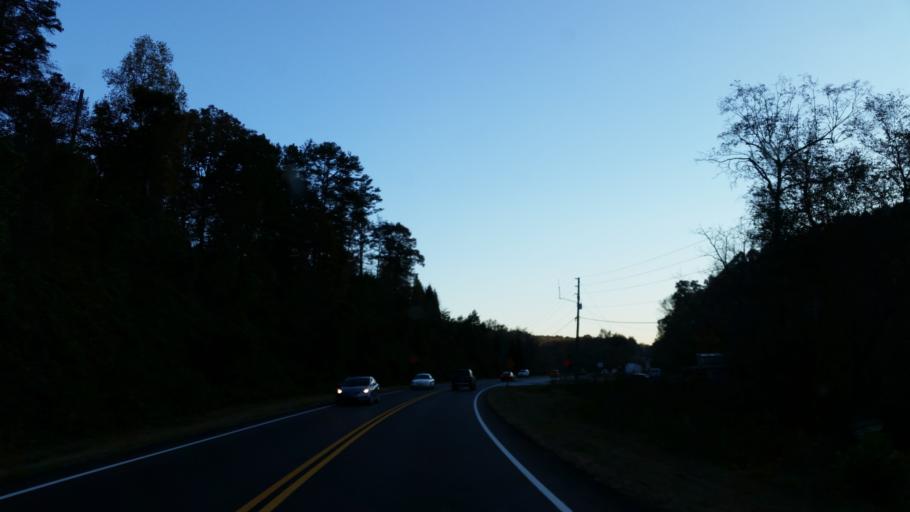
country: US
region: Georgia
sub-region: Lumpkin County
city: Dahlonega
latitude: 34.5028
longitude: -83.9680
